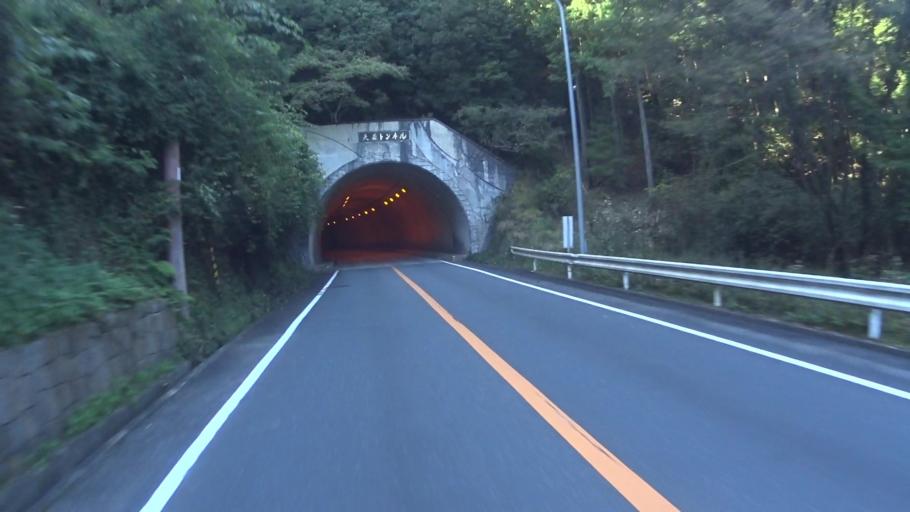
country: JP
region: Kyoto
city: Kameoka
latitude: 35.1370
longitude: 135.5339
